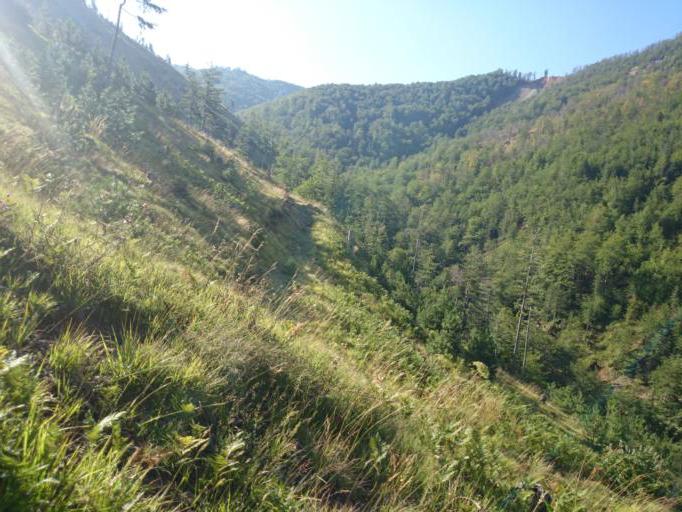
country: AL
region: Diber
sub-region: Rrethi i Bulqizes
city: Martanesh
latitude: 41.4033
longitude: 20.2954
